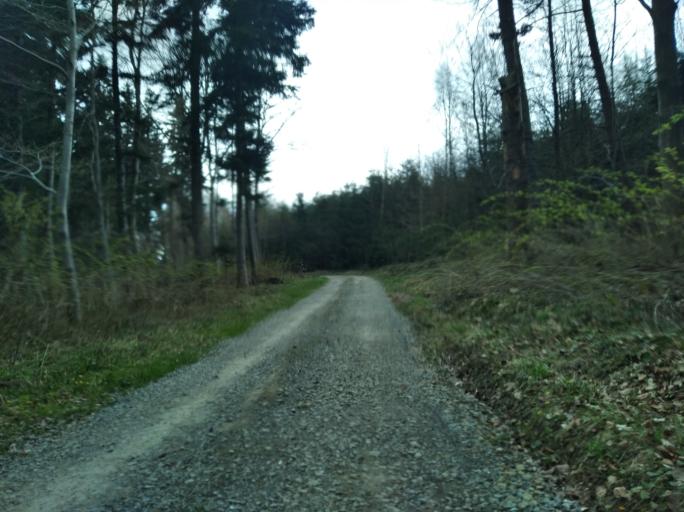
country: PL
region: Subcarpathian Voivodeship
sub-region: Powiat strzyzowski
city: Konieczkowa
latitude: 49.8188
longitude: 21.9362
